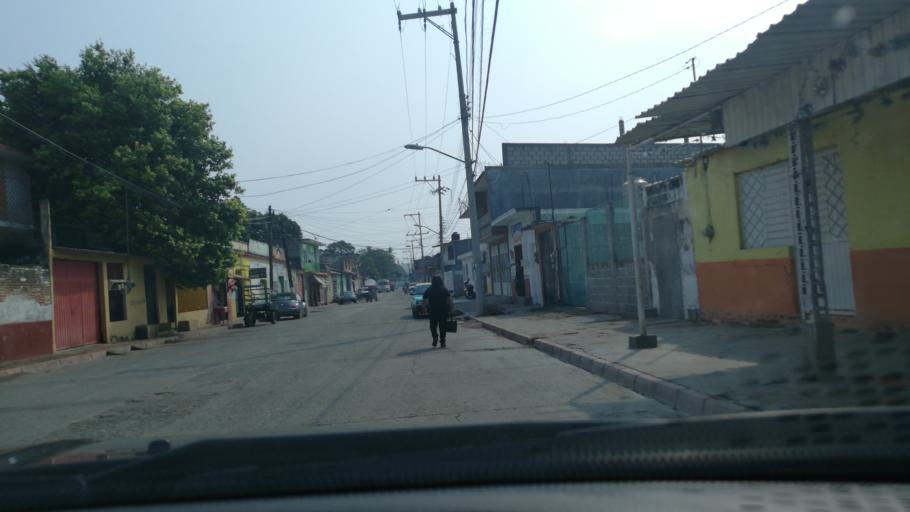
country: MX
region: Oaxaca
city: San Blas Atempa
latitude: 16.3367
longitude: -95.2265
